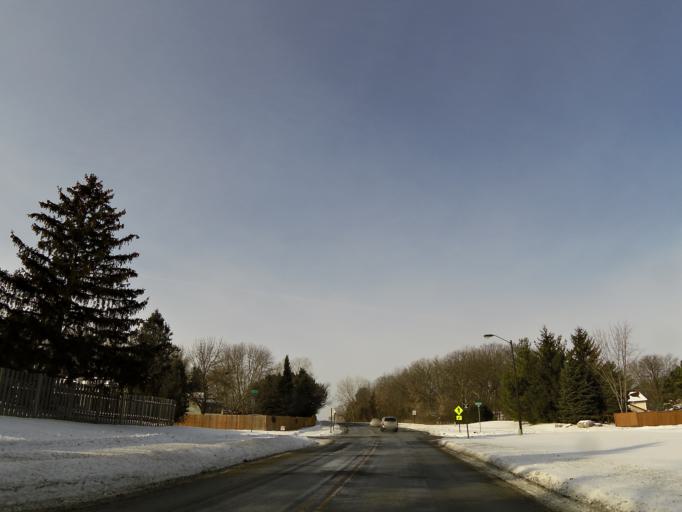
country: US
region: Minnesota
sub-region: Hennepin County
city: Eden Prairie
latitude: 44.8438
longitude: -93.4347
